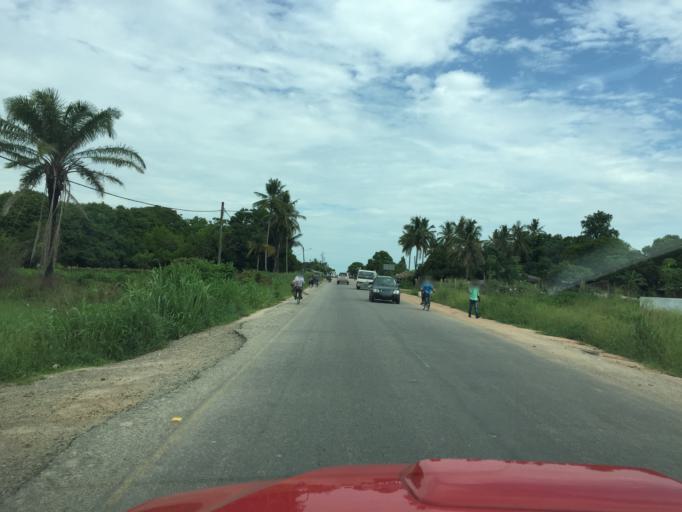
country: MZ
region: Zambezia
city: Quelimane
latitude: -17.5983
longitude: 36.8171
